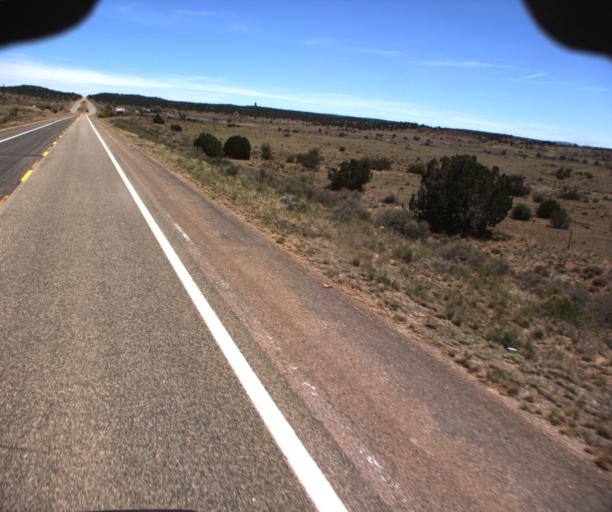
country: US
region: Arizona
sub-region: Mohave County
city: Peach Springs
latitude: 35.5341
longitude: -113.2459
